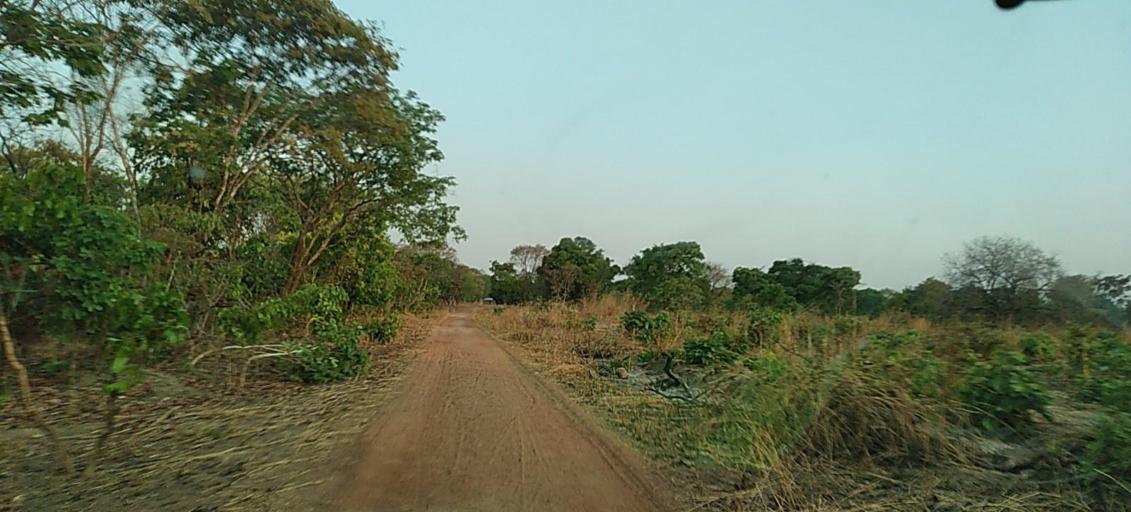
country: ZM
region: North-Western
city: Kalengwa
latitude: -13.1216
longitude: 25.1787
